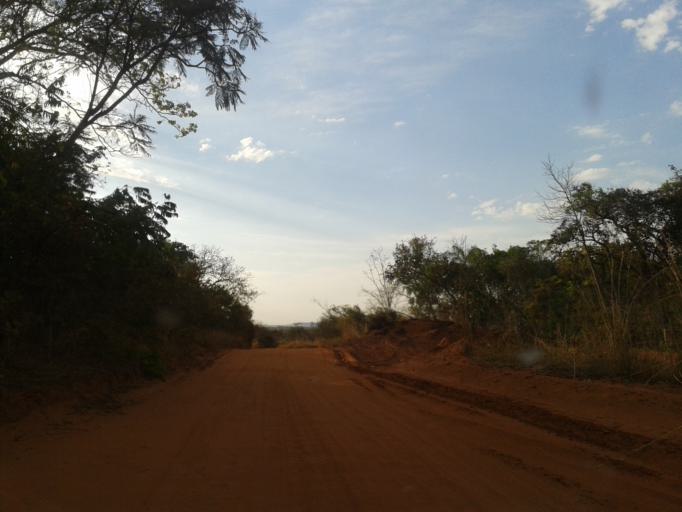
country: BR
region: Minas Gerais
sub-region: Ituiutaba
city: Ituiutaba
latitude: -19.0253
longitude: -49.3492
